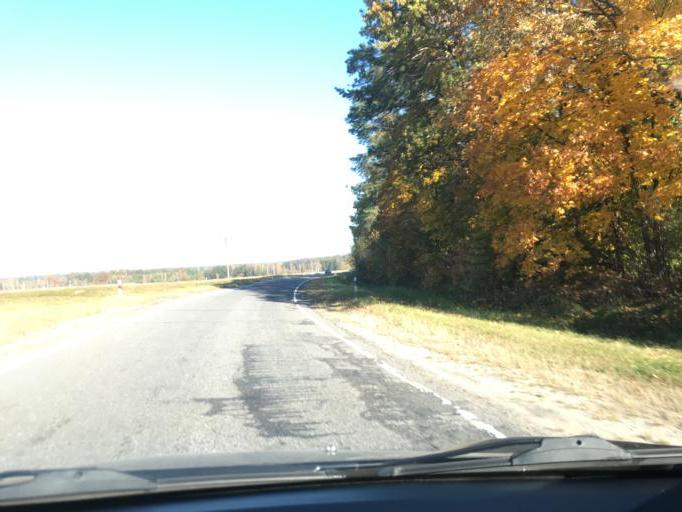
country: BY
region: Gomel
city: Gomel
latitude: 52.3834
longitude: 30.8276
